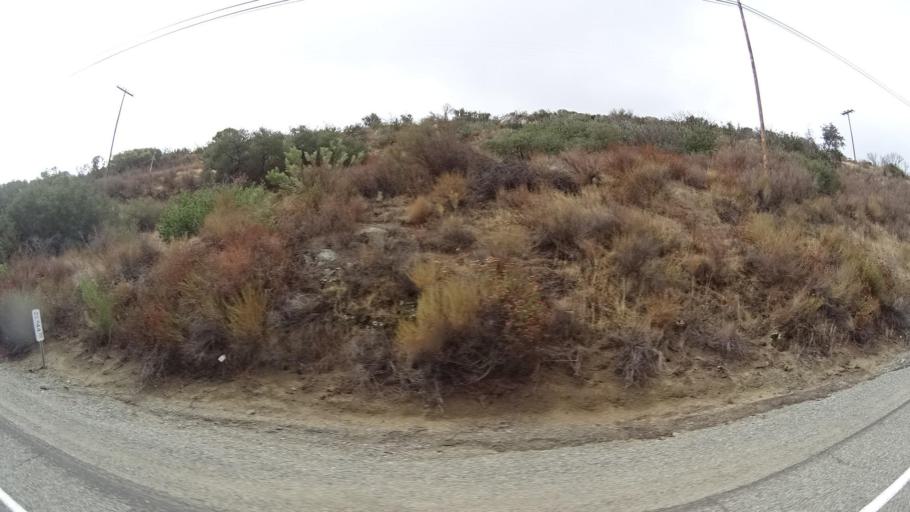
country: MX
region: Baja California
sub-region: Tecate
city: Hacienda Tecate
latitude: 32.5980
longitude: -116.5621
